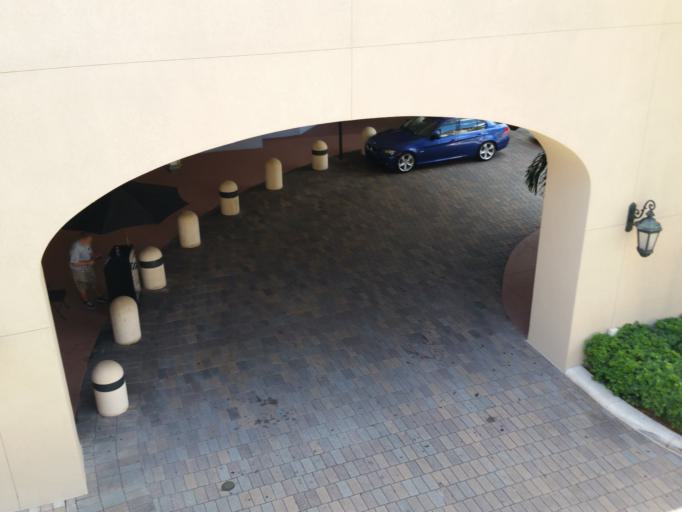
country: US
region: Florida
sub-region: Miami-Dade County
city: Coral Gables
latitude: 25.7319
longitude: -80.2611
